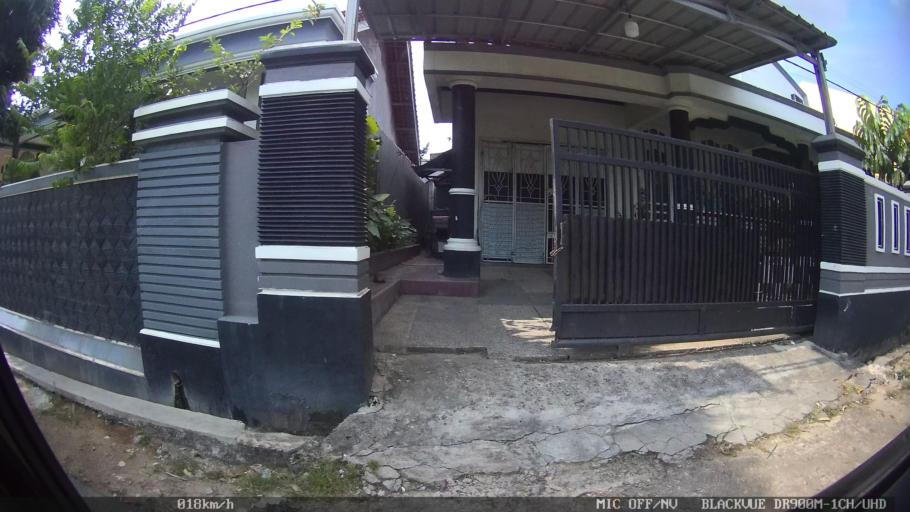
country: ID
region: Lampung
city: Bandarlampung
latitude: -5.4297
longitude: 105.2486
